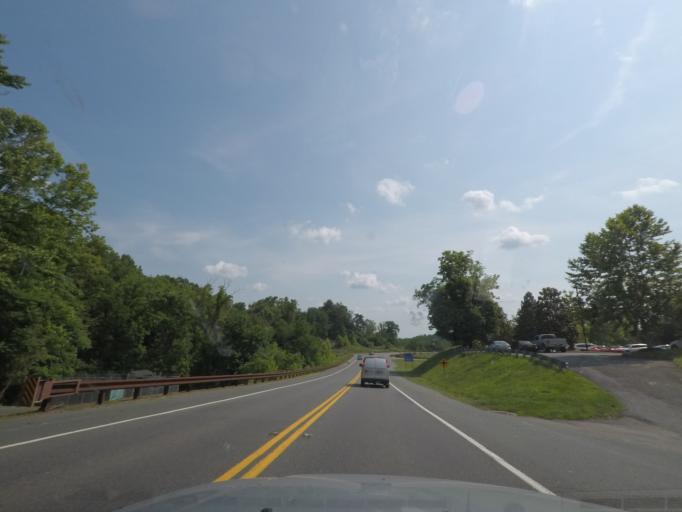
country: US
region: Virginia
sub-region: Fluvanna County
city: Palmyra
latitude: 37.8596
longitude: -78.2639
